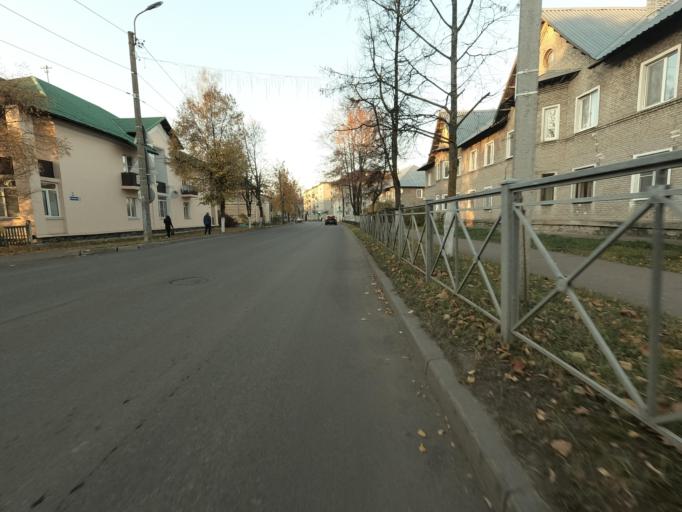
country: RU
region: Leningrad
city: Kirovsk
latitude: 59.8751
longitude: 30.9912
